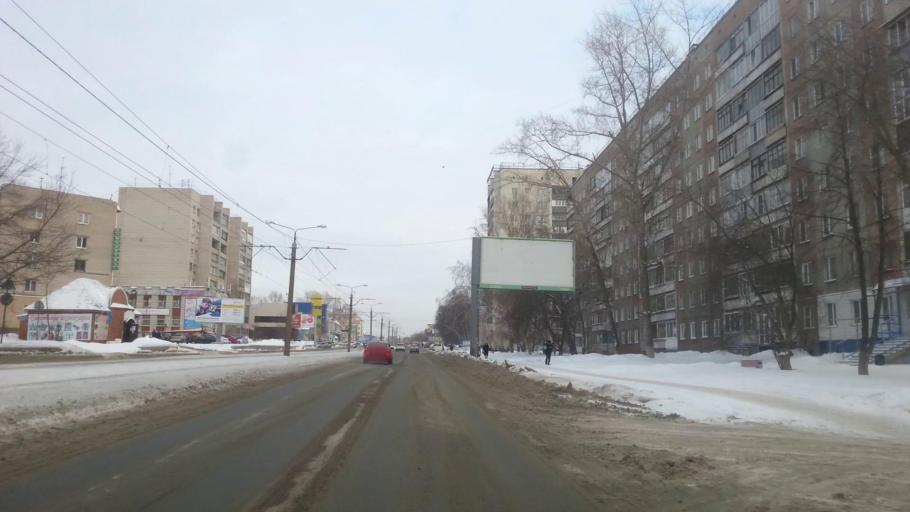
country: RU
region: Altai Krai
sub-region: Gorod Barnaulskiy
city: Barnaul
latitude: 53.3710
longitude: 83.7441
